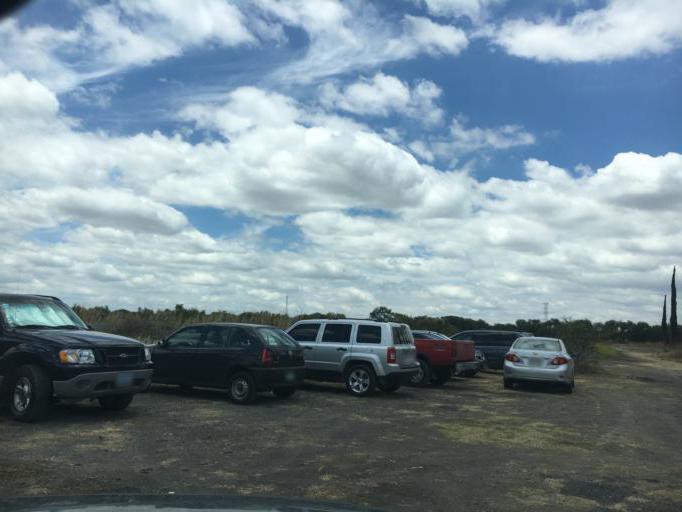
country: MX
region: Guanajuato
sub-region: San Francisco del Rincon
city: Barrio de Guadalupe del Mezquitillo
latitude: 20.9276
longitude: -101.7530
